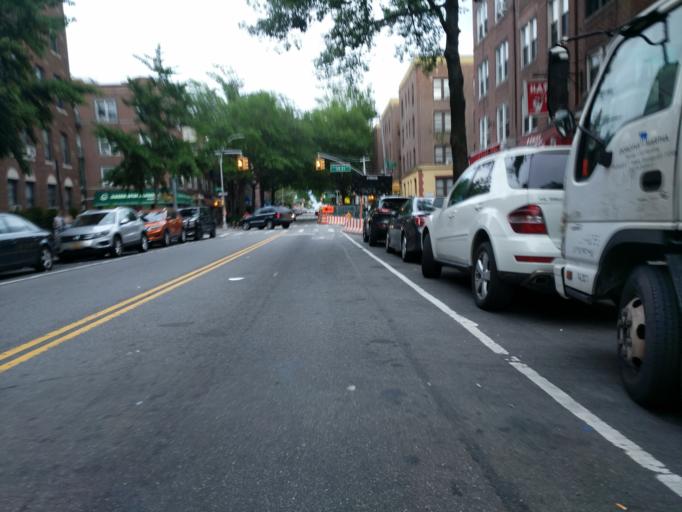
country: US
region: New York
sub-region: Queens County
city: Long Island City
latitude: 40.7630
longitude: -73.9207
